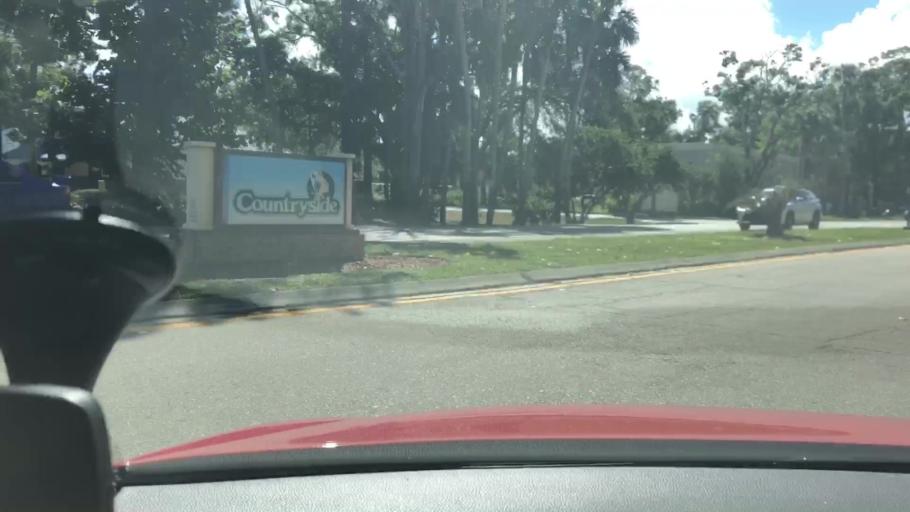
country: US
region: Florida
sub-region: Volusia County
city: Port Orange
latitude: 29.1247
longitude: -81.0037
